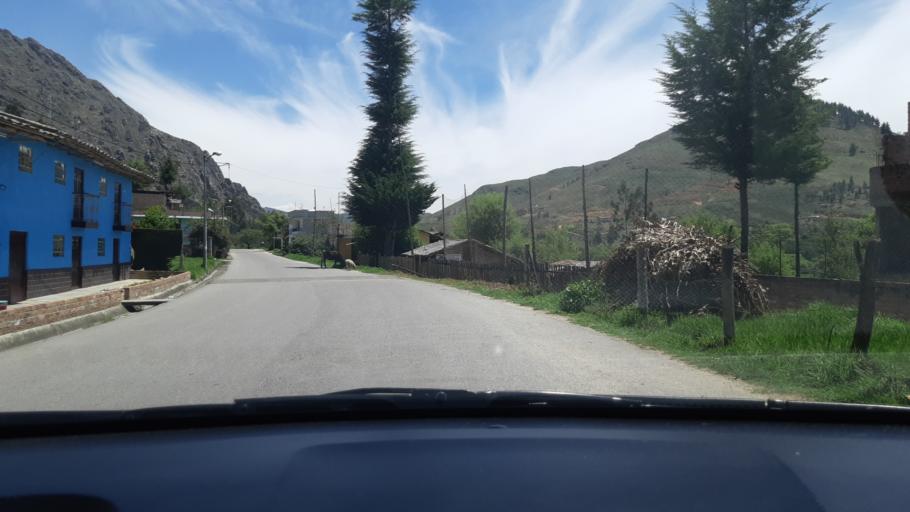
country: PE
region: Cajamarca
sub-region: Provincia de Cajamarca
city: Llacanora
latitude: -7.1815
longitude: -78.4536
